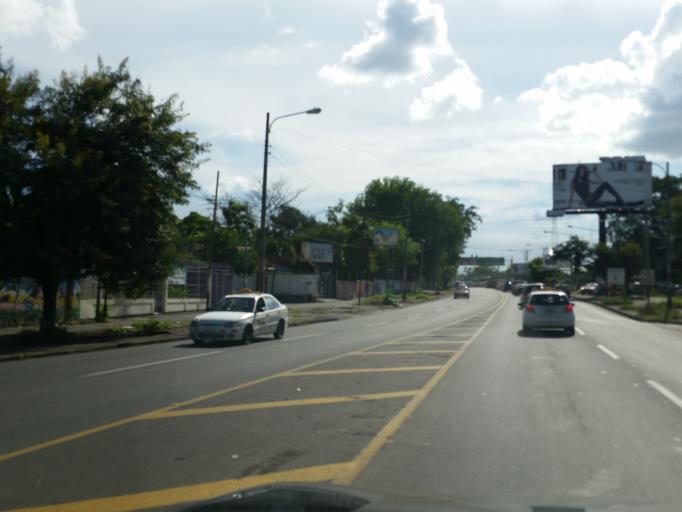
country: NI
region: Managua
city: Managua
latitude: 12.1288
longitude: -86.2676
